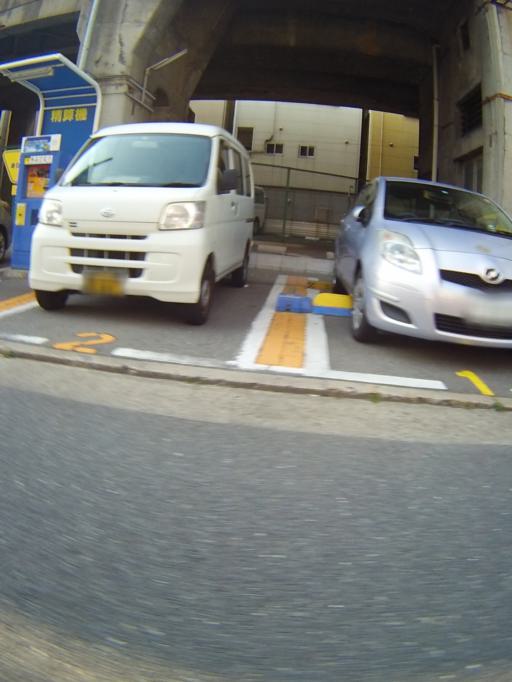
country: JP
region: Osaka
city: Osaka-shi
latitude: 34.6865
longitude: 135.4719
